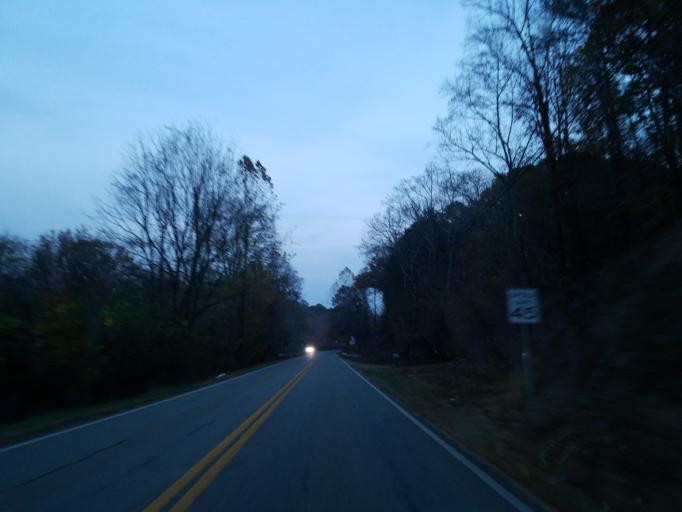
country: US
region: Georgia
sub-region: Pickens County
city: Jasper
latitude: 34.5079
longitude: -84.5091
